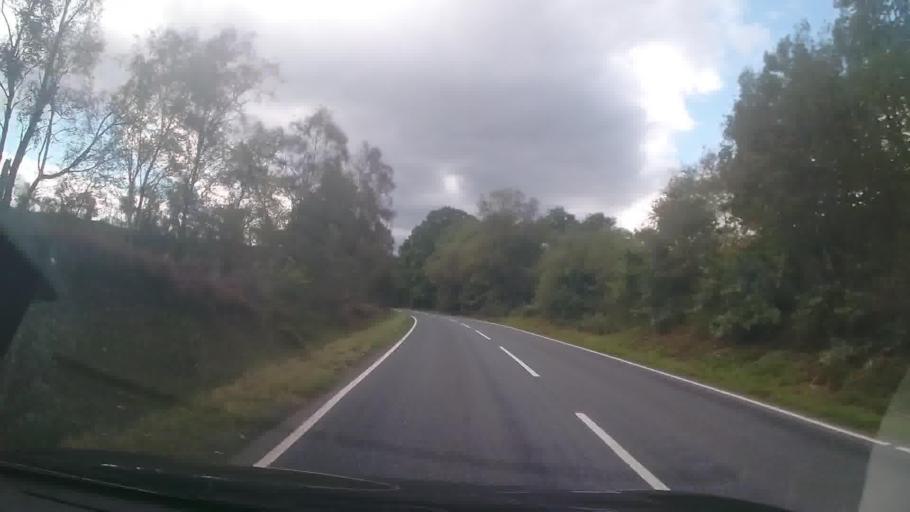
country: GB
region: Scotland
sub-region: Argyll and Bute
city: Garelochhead
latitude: 56.4027
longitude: -5.0167
